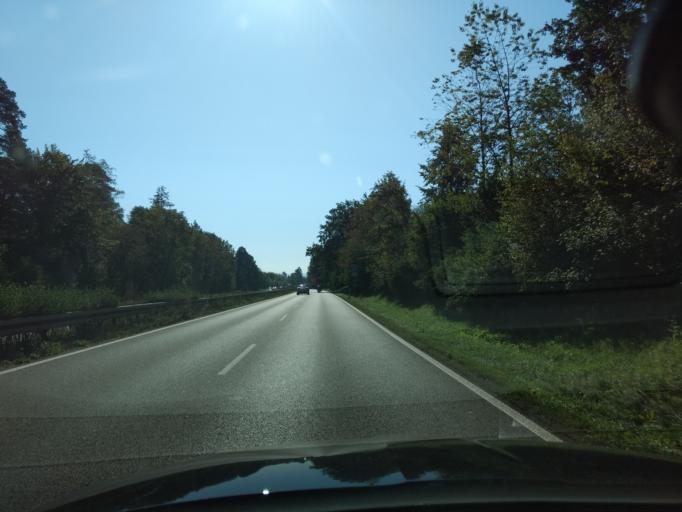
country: DE
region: Bavaria
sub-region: Upper Bavaria
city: Wolfratshausen
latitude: 47.8869
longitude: 11.4524
